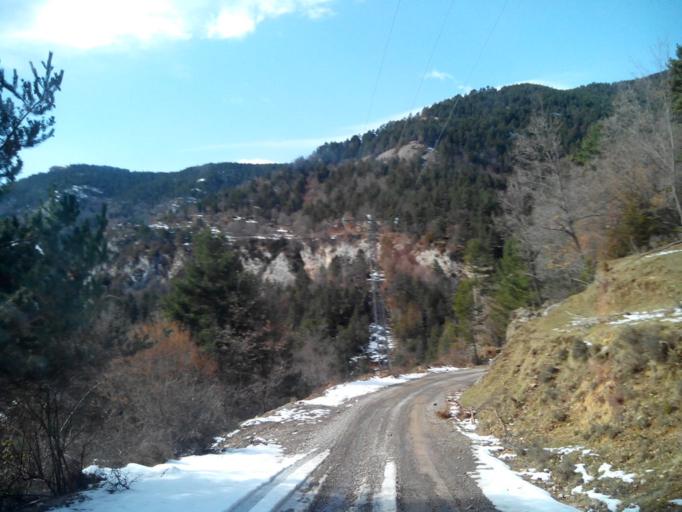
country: ES
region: Catalonia
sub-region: Provincia de Barcelona
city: Vilada
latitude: 42.1839
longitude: 1.9316
